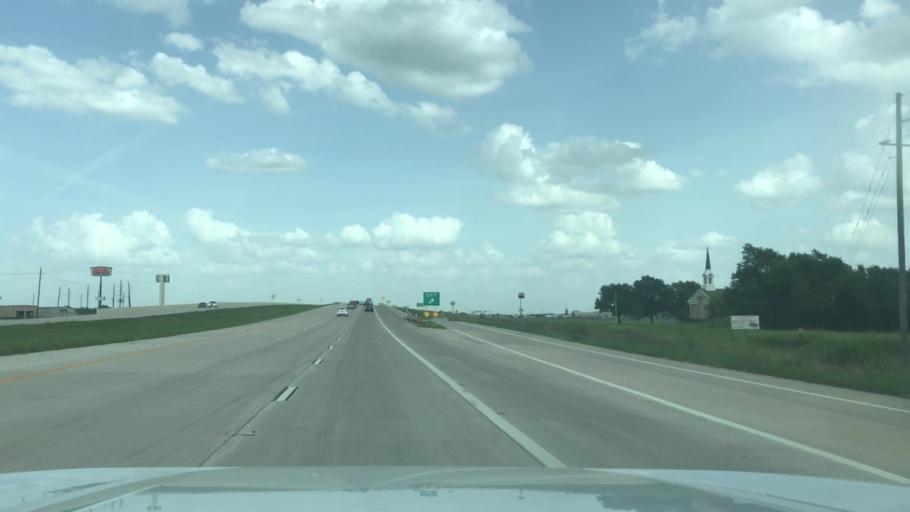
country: US
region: Texas
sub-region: Waller County
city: Waller
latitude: 30.0695
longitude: -95.9275
